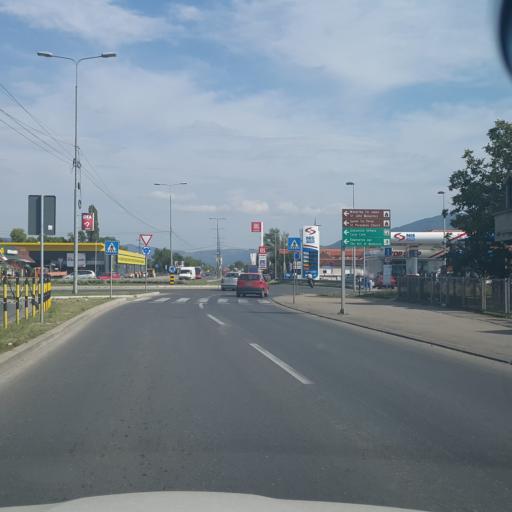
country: RS
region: Central Serbia
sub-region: Nisavski Okrug
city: Nis
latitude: 43.3105
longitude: 21.9341
